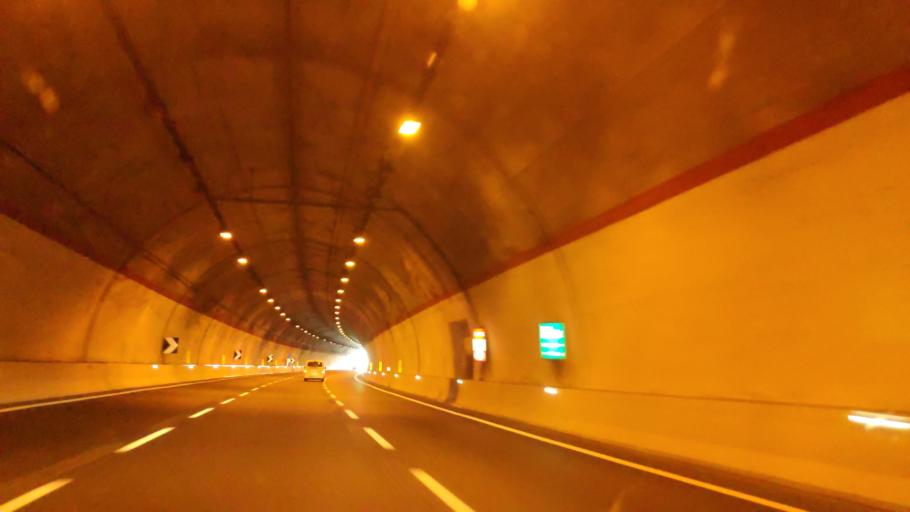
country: IT
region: Campania
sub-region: Provincia di Salerno
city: Contursi Terme
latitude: 40.6149
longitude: 15.2471
